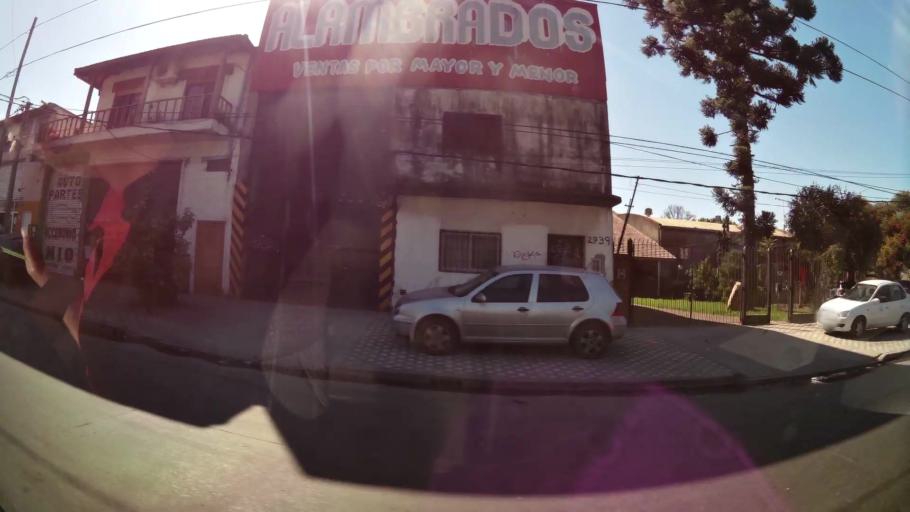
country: AR
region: Buenos Aires
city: Santa Catalina - Dique Lujan
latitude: -34.4923
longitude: -58.7030
